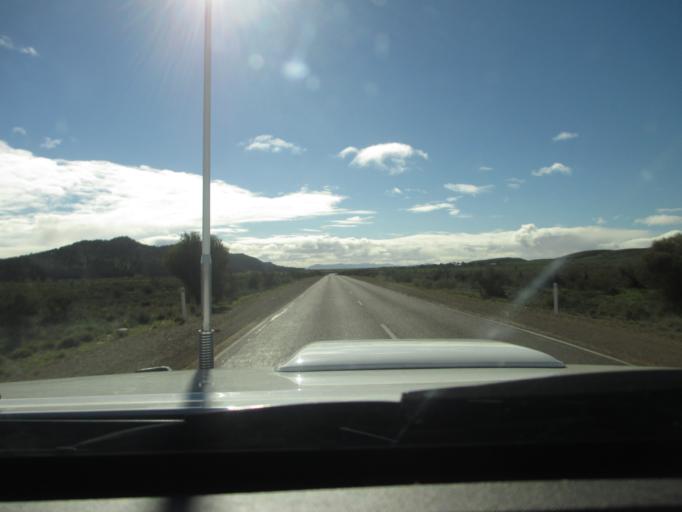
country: AU
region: South Australia
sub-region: Flinders Ranges
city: Quorn
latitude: -31.9444
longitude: 138.4011
